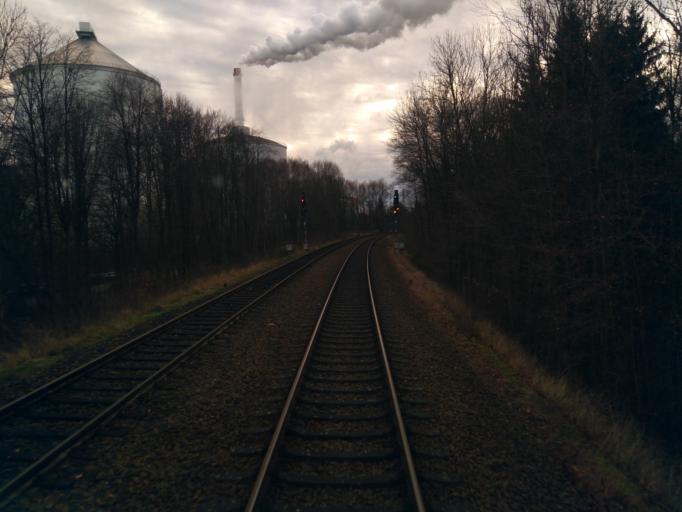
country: DE
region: Lower Saxony
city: Uelzen
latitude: 52.9791
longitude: 10.5528
